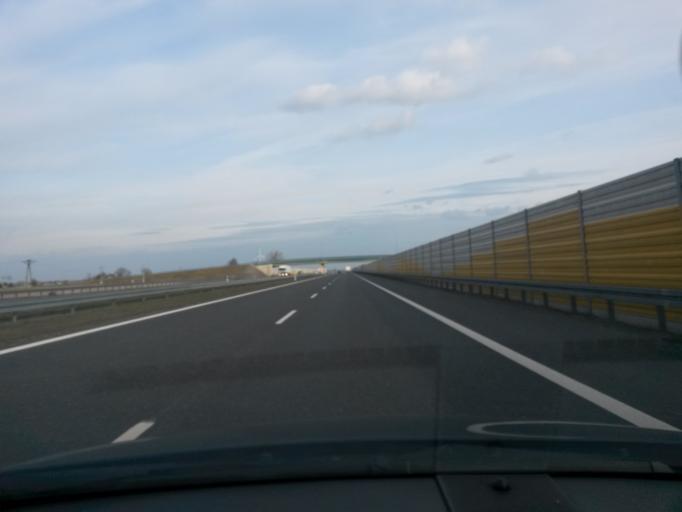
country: PL
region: Lodz Voivodeship
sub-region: Powiat leczycki
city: Swinice Warckie
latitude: 52.0199
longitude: 18.9342
